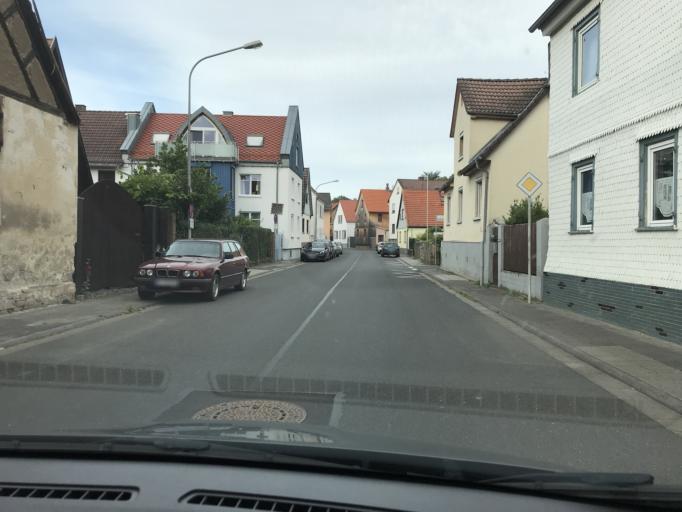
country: DE
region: Hesse
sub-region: Regierungsbezirk Darmstadt
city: Schaafheim
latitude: 49.9129
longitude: 8.9743
